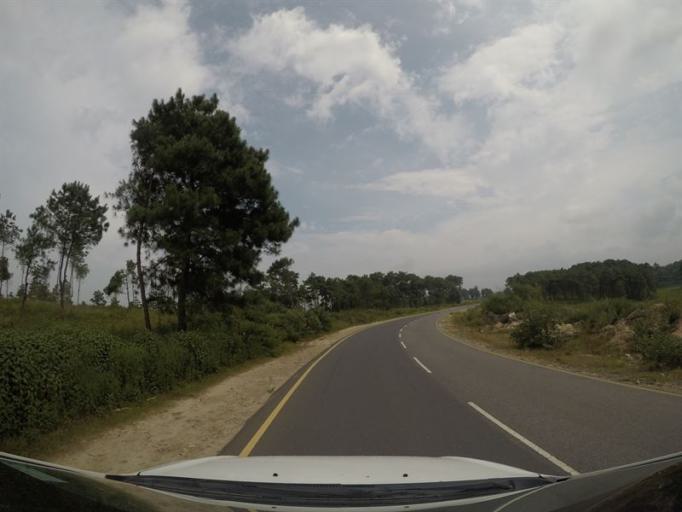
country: IN
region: Meghalaya
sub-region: East Khasi Hills
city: Shillong
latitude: 25.4904
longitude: 92.1888
